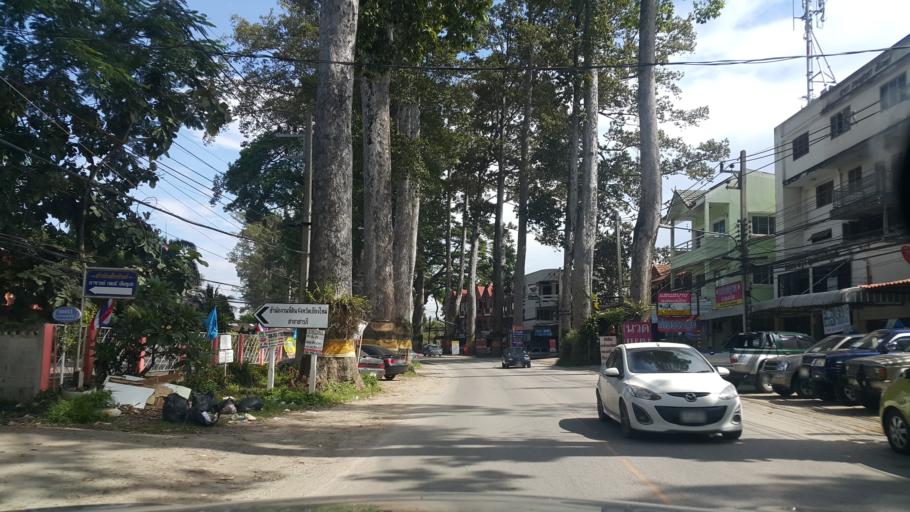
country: TH
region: Chiang Mai
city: Saraphi
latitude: 18.7343
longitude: 99.0170
